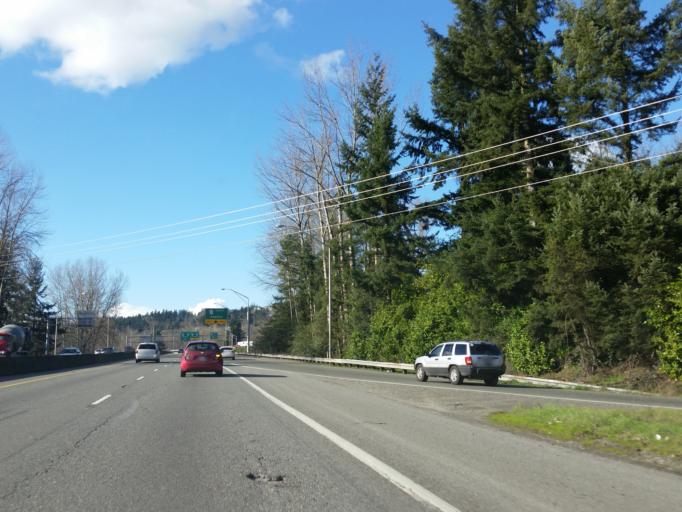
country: US
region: Washington
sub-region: Pierce County
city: Sumner
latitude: 47.1995
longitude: -122.2514
